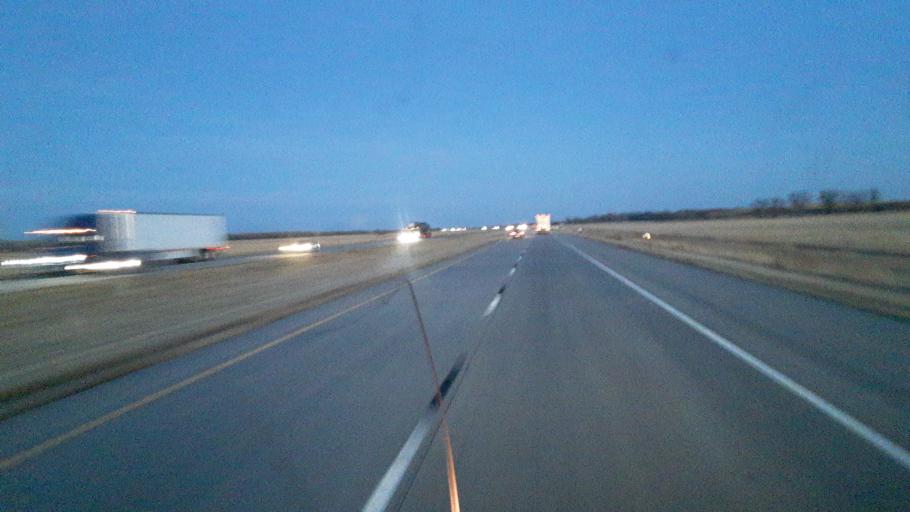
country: US
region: Nebraska
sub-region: Lincoln County
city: Sutherland
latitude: 41.1085
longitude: -101.4144
